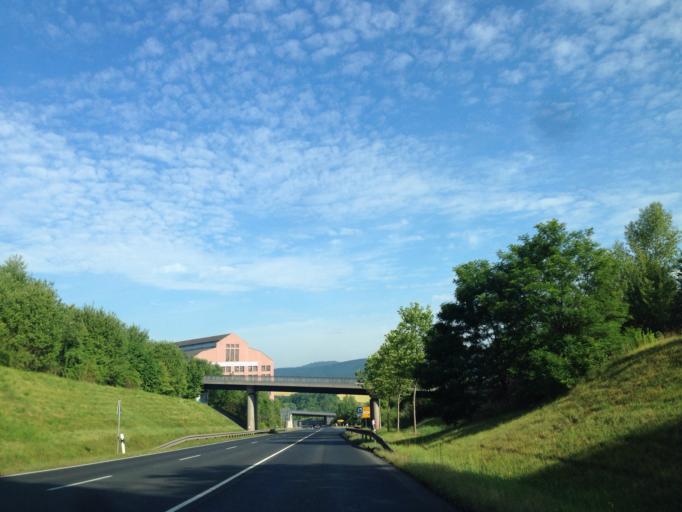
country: DE
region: Thuringia
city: Unterwellenborn
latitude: 50.6541
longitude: 11.4297
